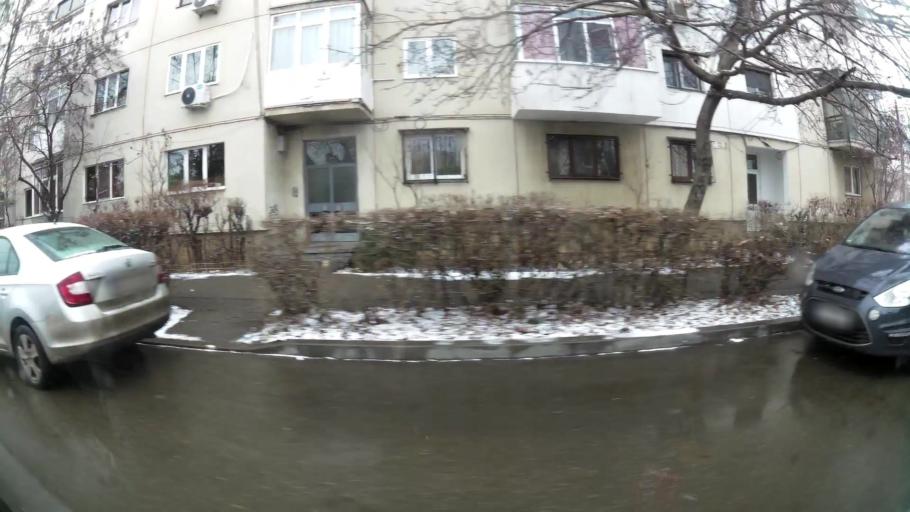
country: RO
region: Prahova
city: Ploiesti
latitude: 44.9398
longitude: 26.0002
